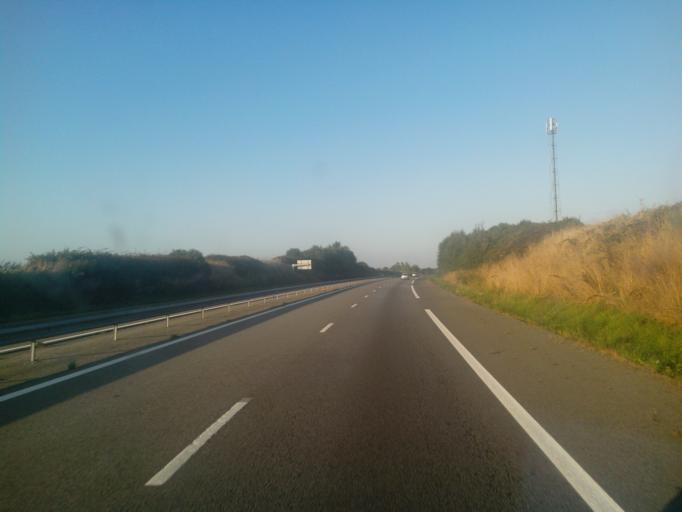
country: FR
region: Brittany
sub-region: Departement du Morbihan
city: Saint-Gonnery
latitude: 48.1269
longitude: -2.8410
